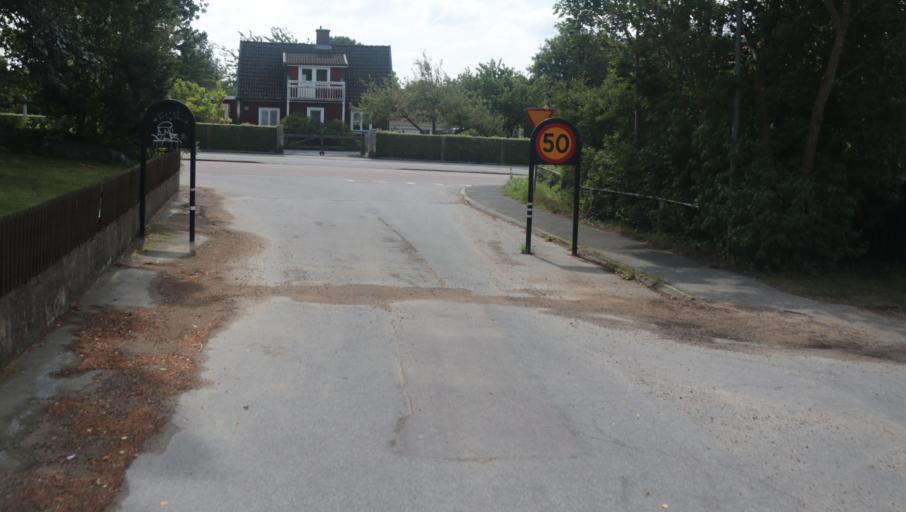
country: SE
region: Blekinge
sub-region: Karlshamns Kommun
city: Karlshamn
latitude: 56.2093
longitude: 14.8374
